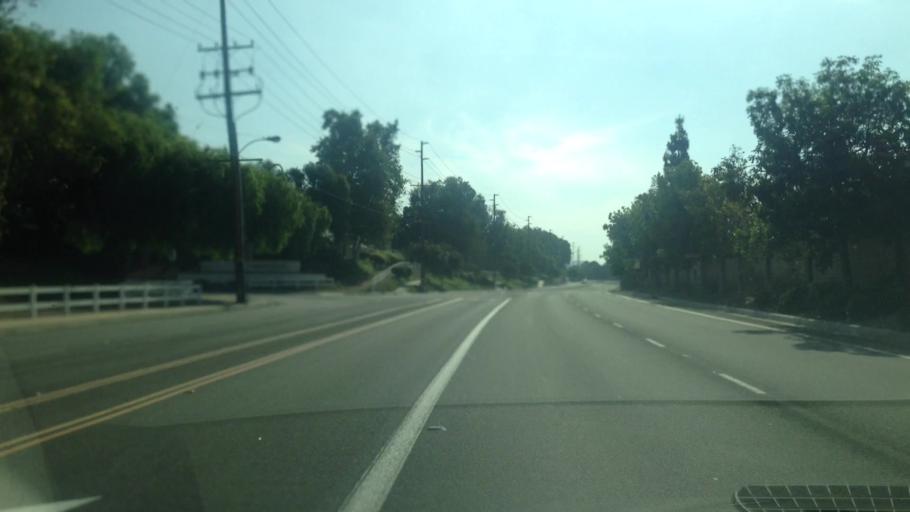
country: US
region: California
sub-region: Orange County
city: Yorba Linda
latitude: 33.8742
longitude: -117.7663
